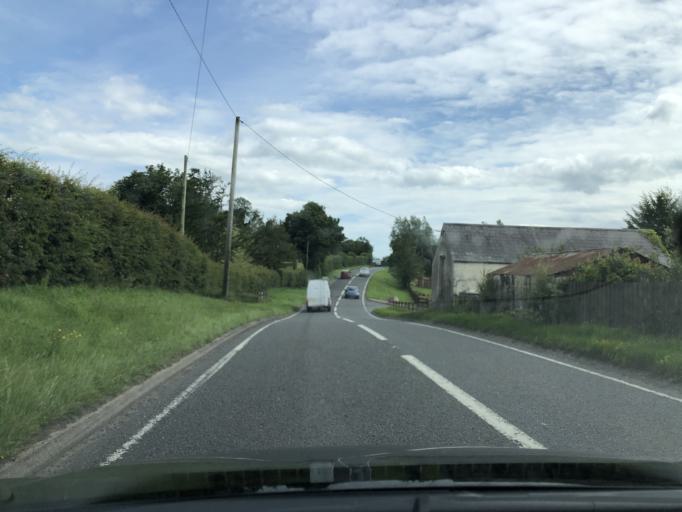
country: GB
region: Northern Ireland
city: Ballynahinch
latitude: 54.4282
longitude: -5.9261
